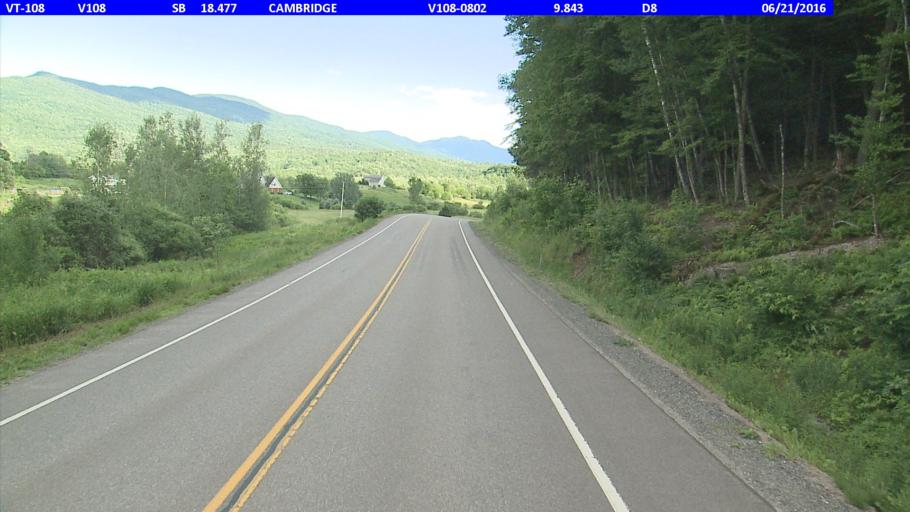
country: US
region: Vermont
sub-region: Lamoille County
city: Johnson
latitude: 44.6581
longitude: -72.8294
